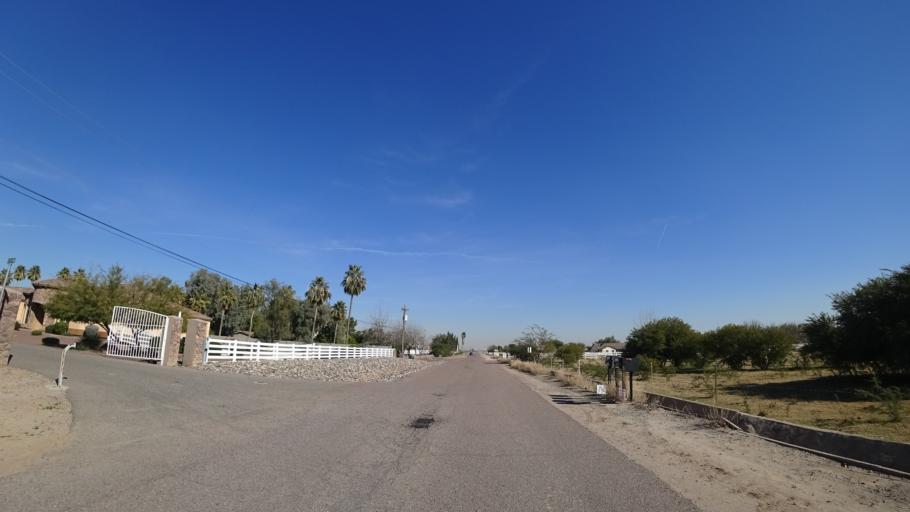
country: US
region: Arizona
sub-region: Maricopa County
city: Citrus Park
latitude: 33.5300
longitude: -112.4321
